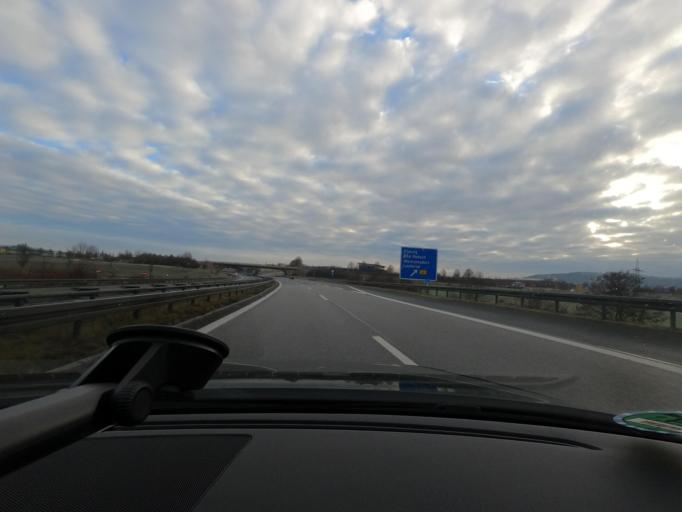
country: DE
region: Bavaria
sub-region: Upper Franconia
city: Coburg
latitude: 50.2911
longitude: 10.9739
